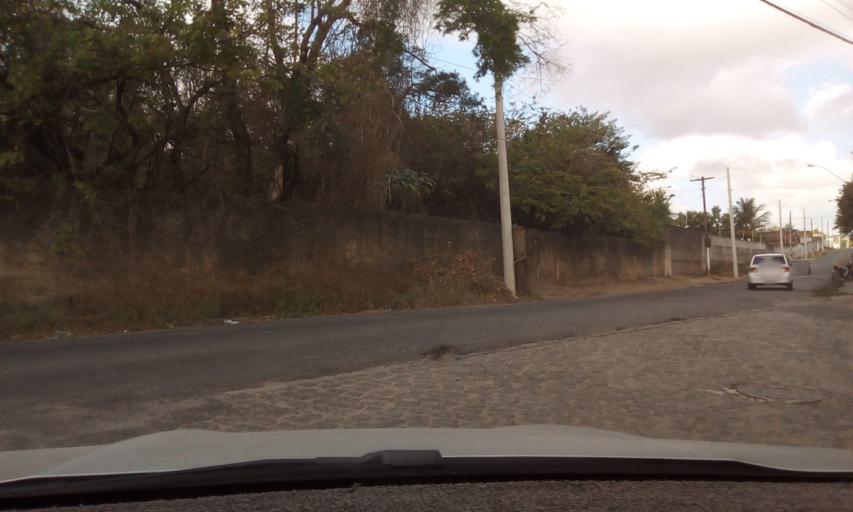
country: BR
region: Paraiba
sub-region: Bayeux
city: Bayeux
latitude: -7.1510
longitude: -34.9031
